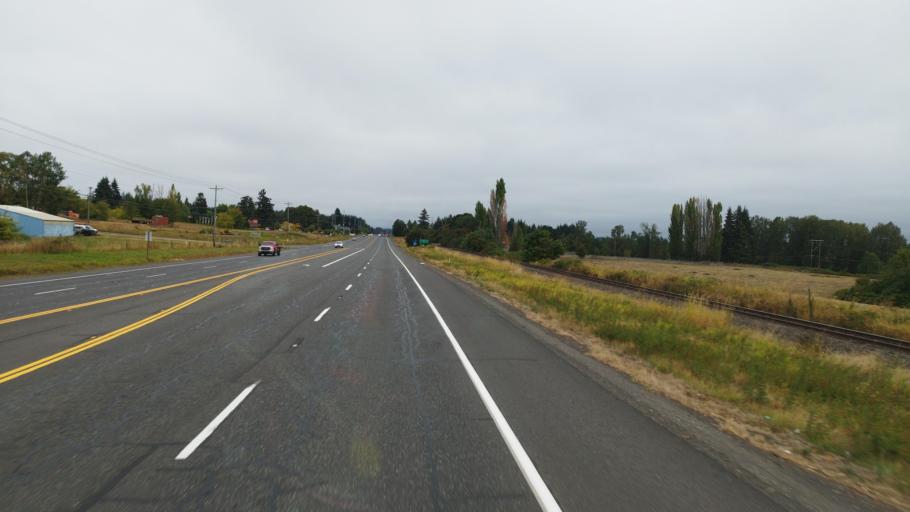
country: US
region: Oregon
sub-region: Columbia County
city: Warren
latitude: 45.8046
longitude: -122.8594
